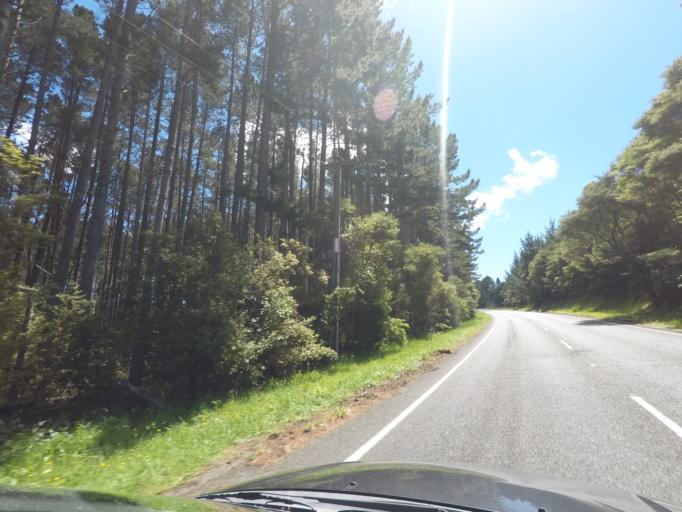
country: NZ
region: Auckland
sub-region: Auckland
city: Rothesay Bay
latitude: -36.7432
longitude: 174.6741
